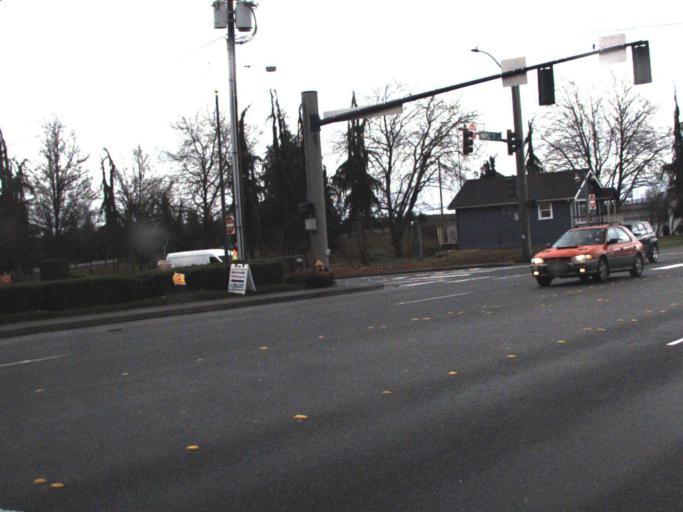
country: US
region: Washington
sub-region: Snohomish County
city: Everett
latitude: 47.9806
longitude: -122.1910
